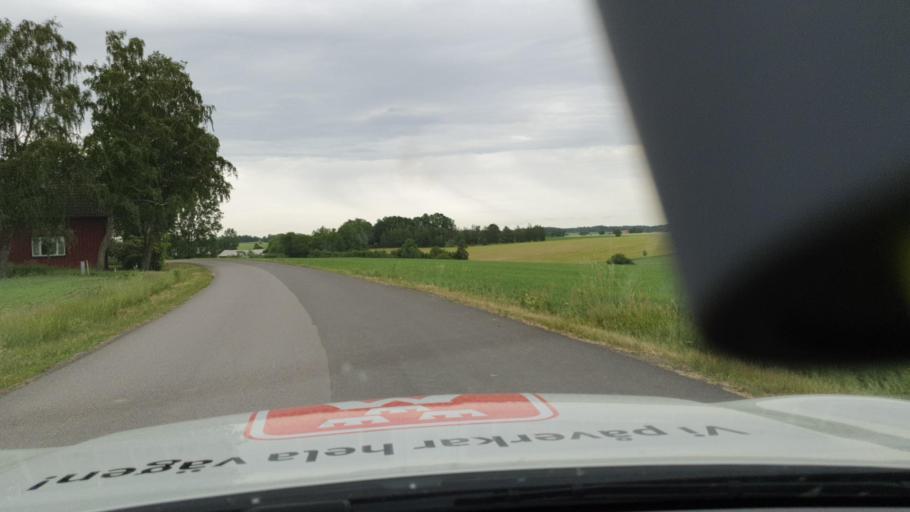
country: SE
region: Vaestra Goetaland
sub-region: Skovde Kommun
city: Skoevde
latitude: 58.3834
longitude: 13.9006
